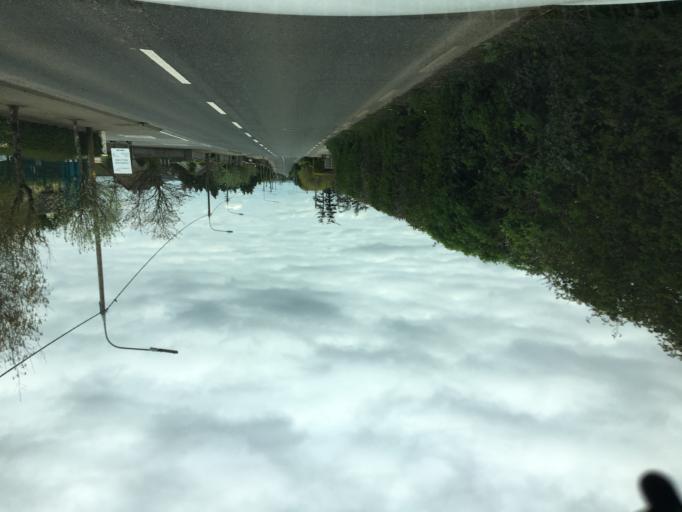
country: IE
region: Leinster
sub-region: Loch Garman
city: Enniscorthy
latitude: 52.4504
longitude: -6.7153
